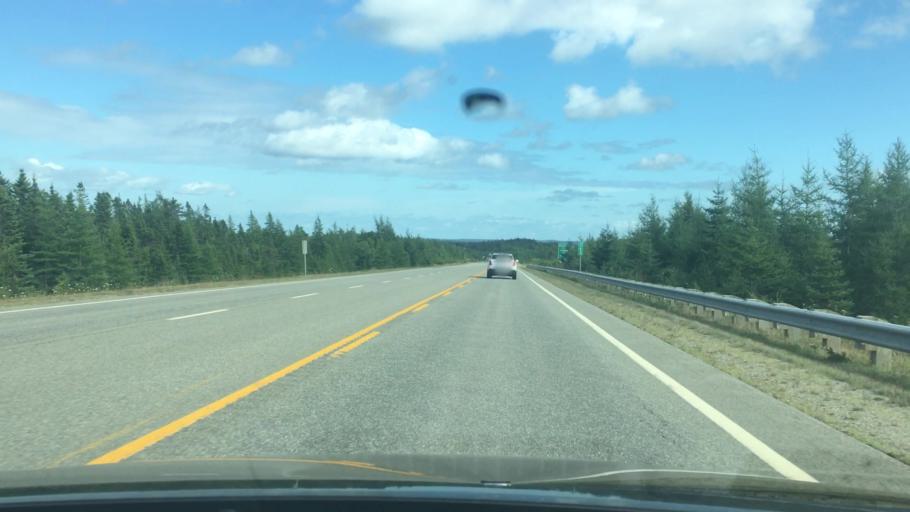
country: CA
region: Nova Scotia
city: Port Hawkesbury
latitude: 45.6190
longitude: -61.1103
